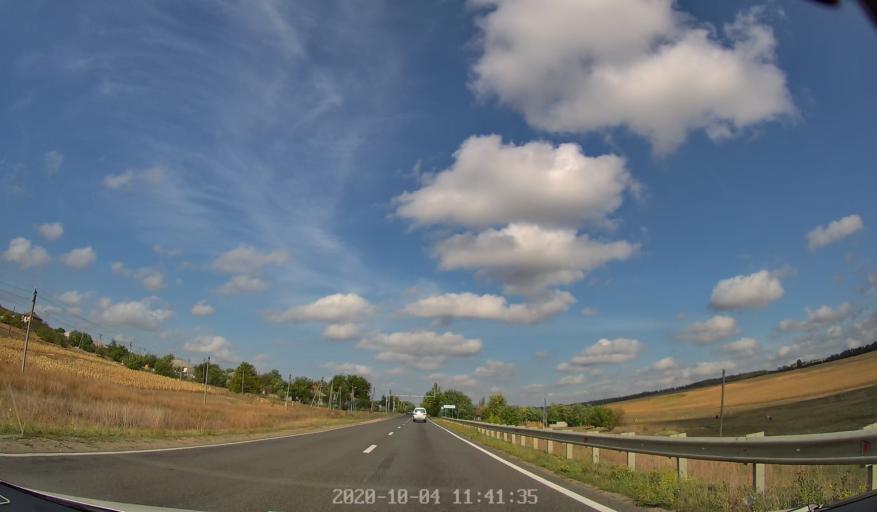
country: MD
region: Orhei
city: Orhei
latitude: 47.4201
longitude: 28.8075
